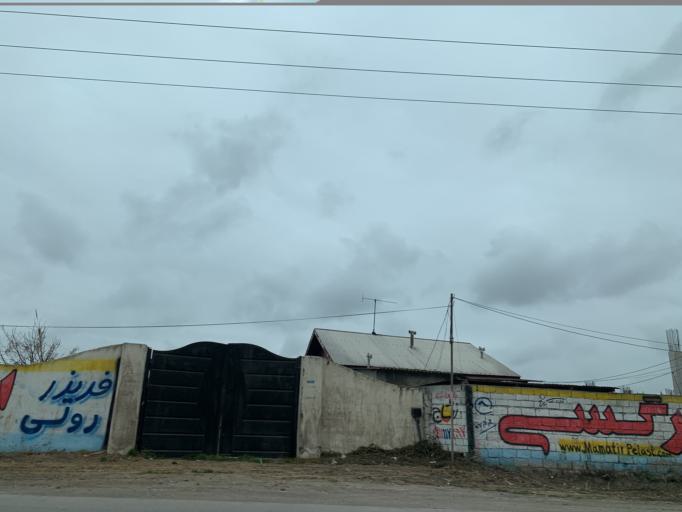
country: IR
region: Mazandaran
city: Babol
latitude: 36.5157
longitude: 52.5716
